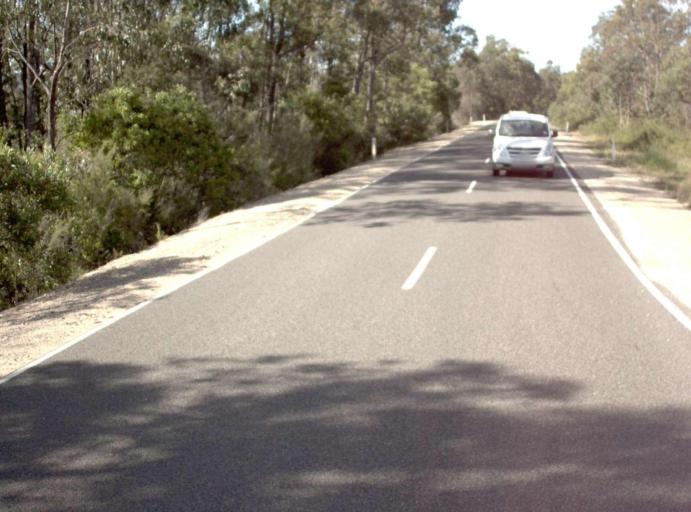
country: AU
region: Victoria
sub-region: East Gippsland
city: Lakes Entrance
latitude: -37.5753
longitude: 148.1272
